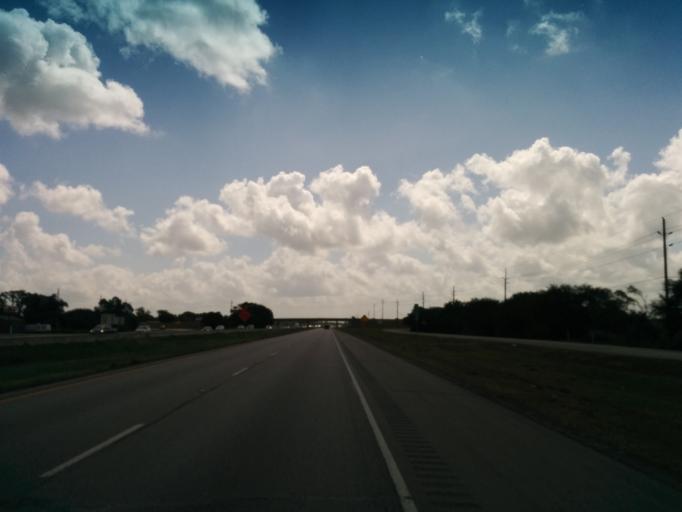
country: US
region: Texas
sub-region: Austin County
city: Sealy
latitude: 29.7758
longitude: -96.1135
